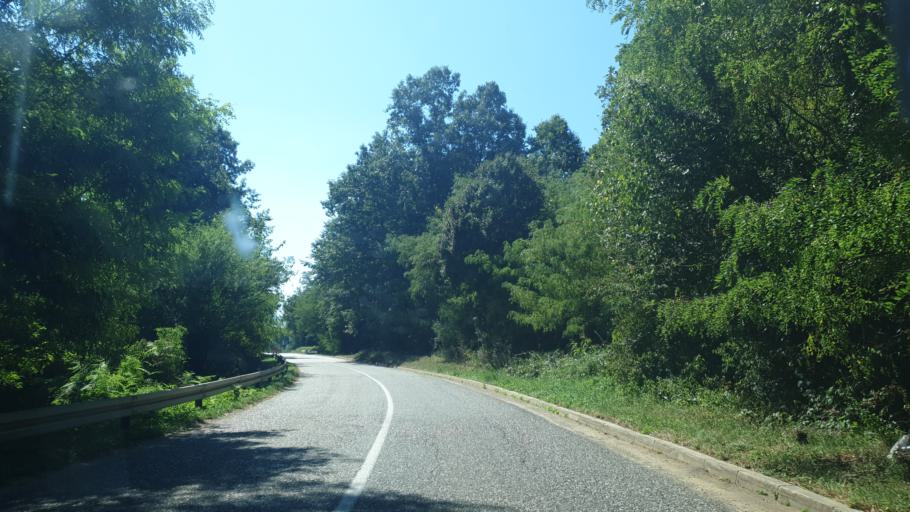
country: RS
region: Central Serbia
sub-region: Kolubarski Okrug
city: Mionica
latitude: 44.1994
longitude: 20.0792
